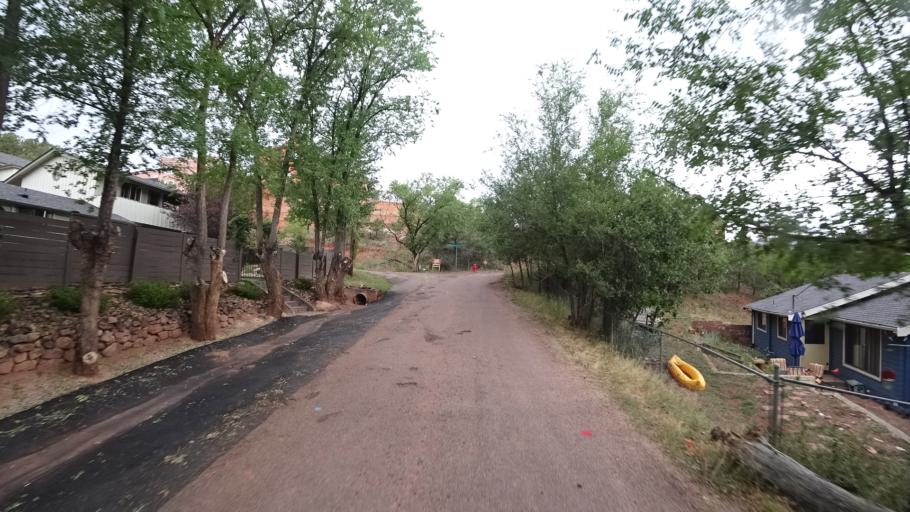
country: US
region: Colorado
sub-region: El Paso County
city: Manitou Springs
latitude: 38.8505
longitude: -104.8979
